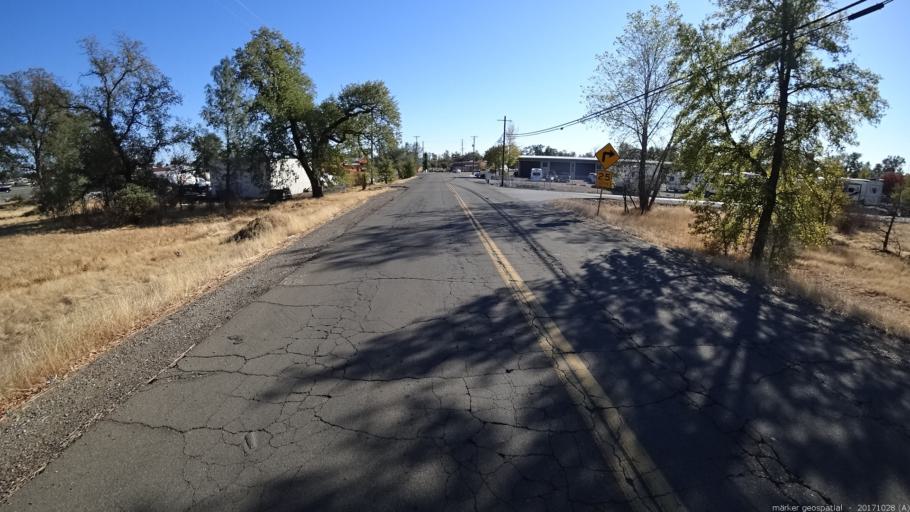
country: US
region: California
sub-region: Shasta County
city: Shasta Lake
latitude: 40.6404
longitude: -122.3671
